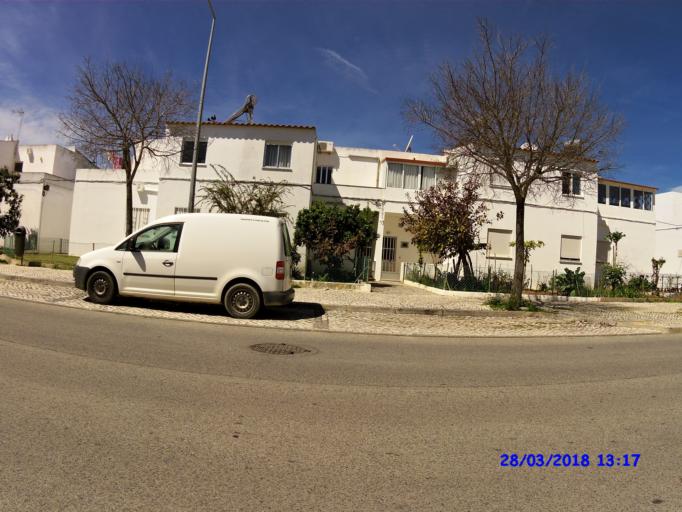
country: PT
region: Faro
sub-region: Albufeira
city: Ferreiras
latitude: 37.1273
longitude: -8.2343
